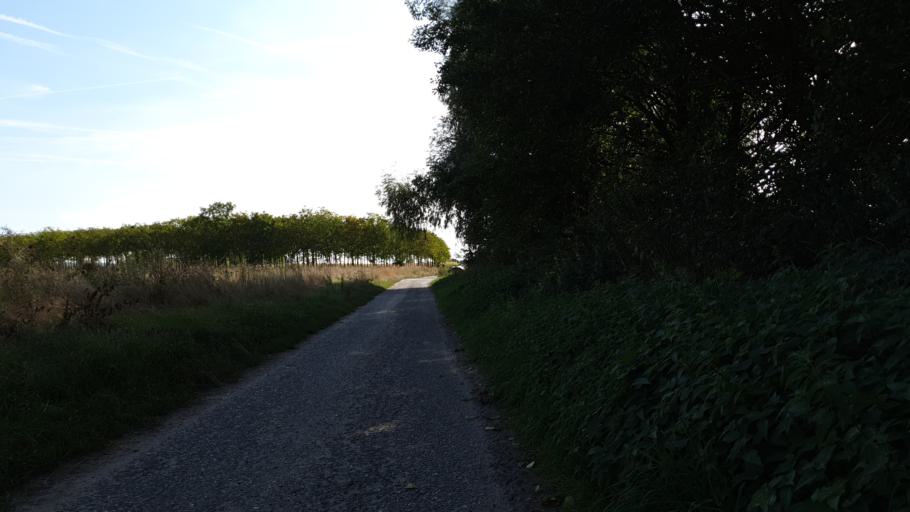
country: DE
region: Rheinland-Pfalz
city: Hergersweiler
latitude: 49.1025
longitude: 8.0948
